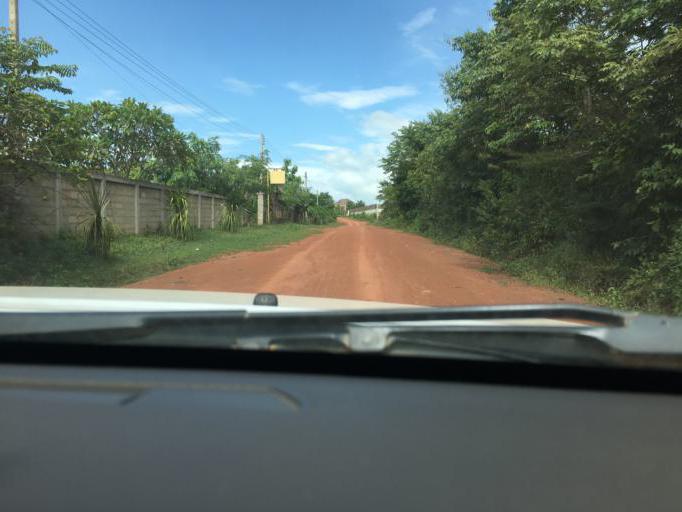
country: LA
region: Xiagnabouli
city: Muang Kenthao
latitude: 17.7102
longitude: 101.4068
